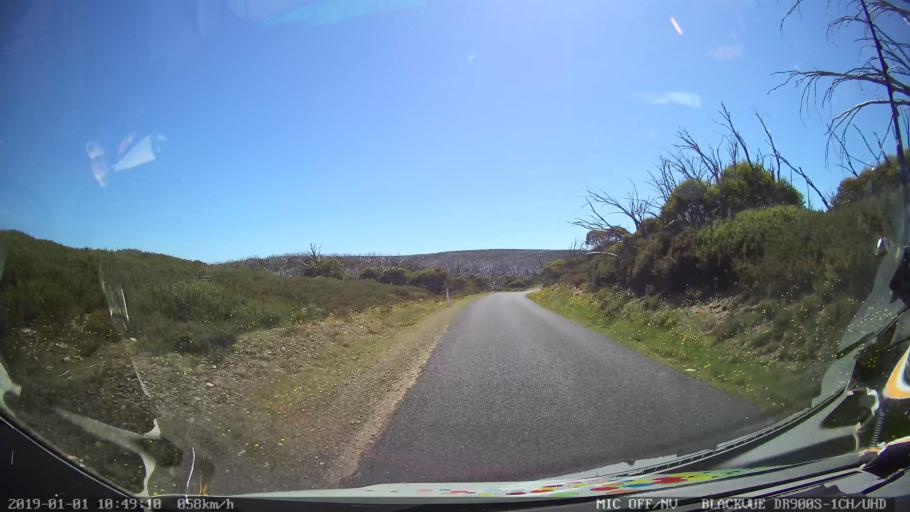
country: AU
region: New South Wales
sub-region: Snowy River
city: Jindabyne
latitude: -36.0362
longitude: 148.3670
